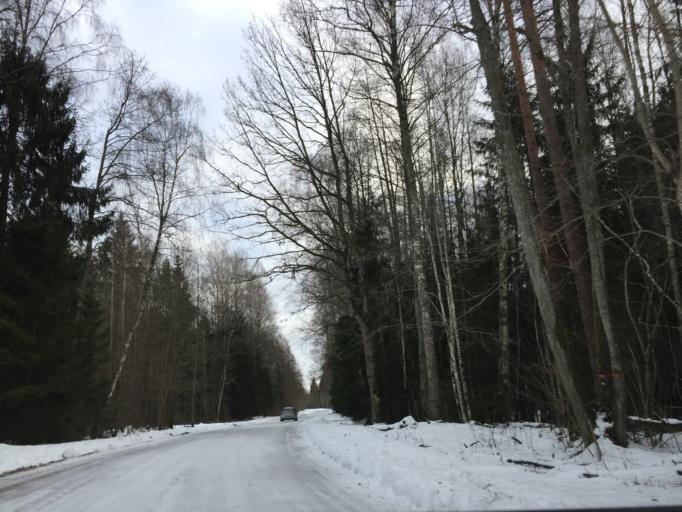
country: LV
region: Lielvarde
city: Lielvarde
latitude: 56.5817
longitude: 24.7591
